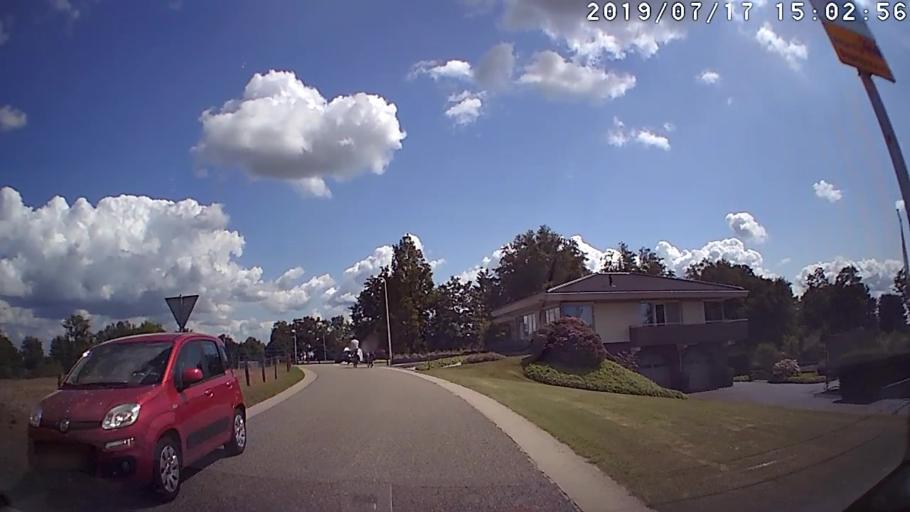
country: NL
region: Overijssel
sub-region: Gemeente Kampen
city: Kampen
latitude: 52.5179
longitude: 5.9570
